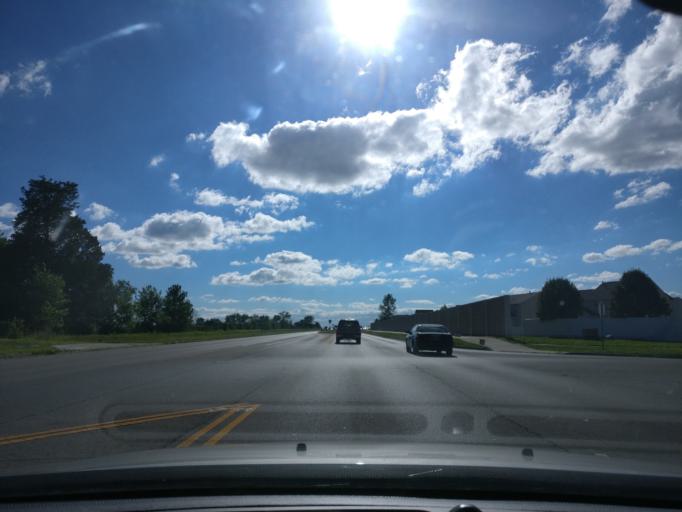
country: US
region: Ohio
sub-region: Warren County
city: Five Points
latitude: 39.5977
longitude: -84.2117
